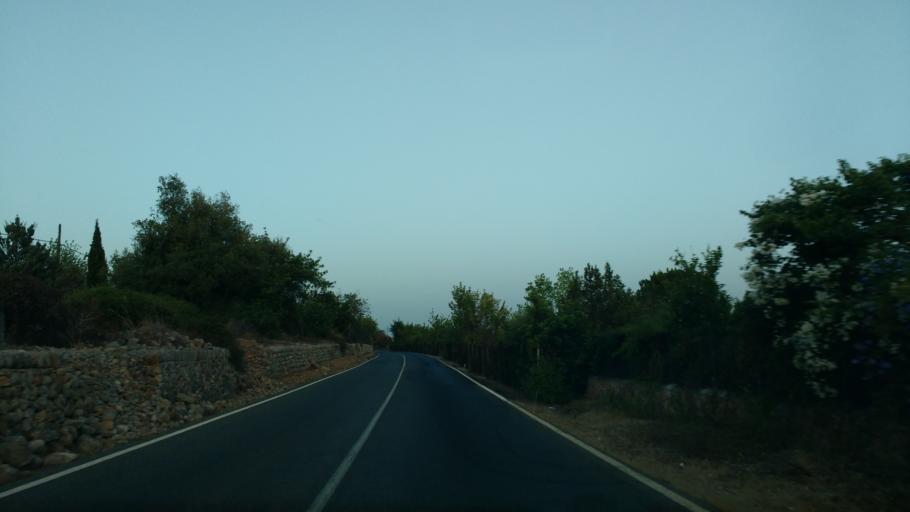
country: ES
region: Balearic Islands
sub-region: Illes Balears
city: Bunyola
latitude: 39.6665
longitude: 2.6884
